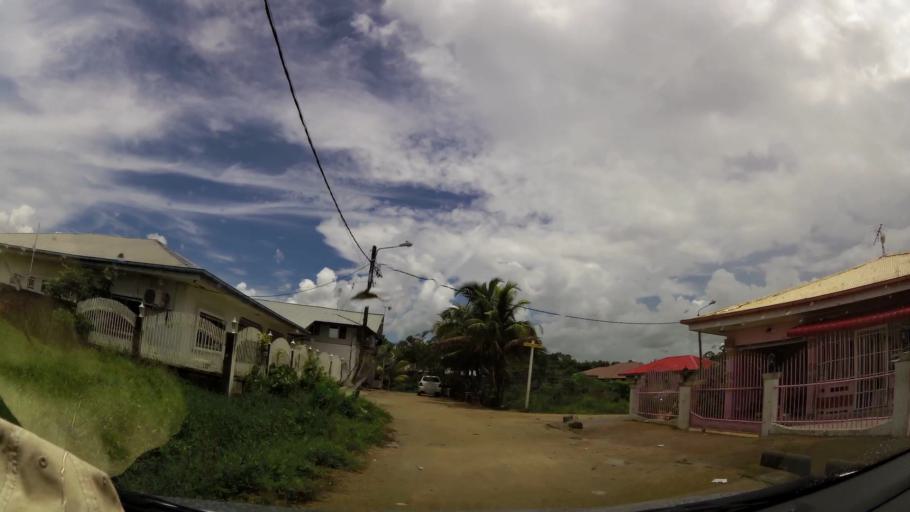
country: SR
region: Wanica
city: Lelydorp
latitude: 5.7895
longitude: -55.2202
